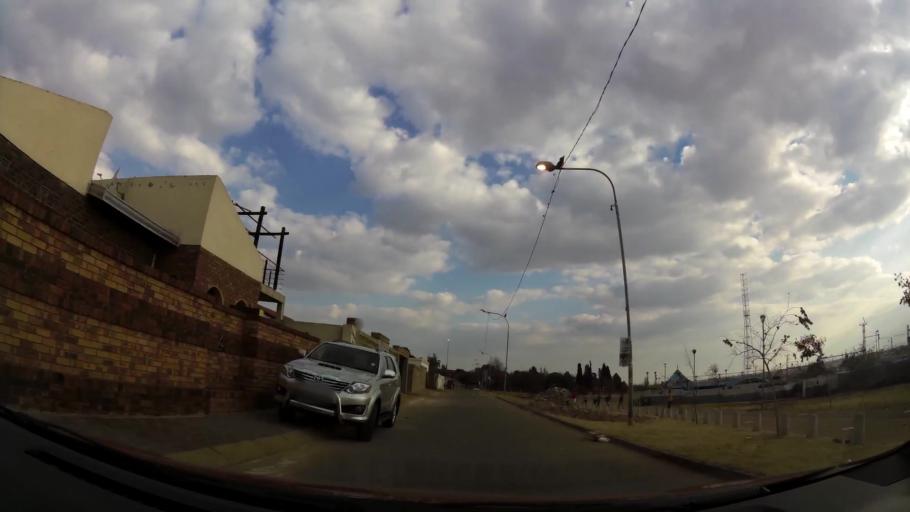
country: ZA
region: Gauteng
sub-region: City of Johannesburg Metropolitan Municipality
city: Soweto
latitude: -26.2260
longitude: 27.9293
